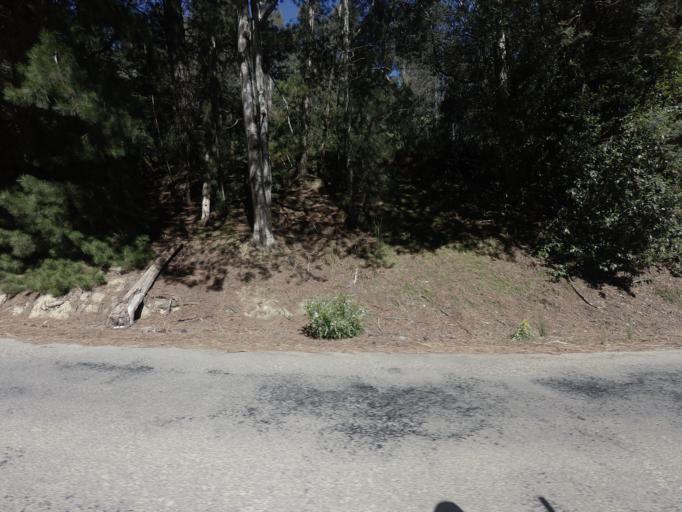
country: AU
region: Tasmania
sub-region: Derwent Valley
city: New Norfolk
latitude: -42.7627
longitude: 146.6029
